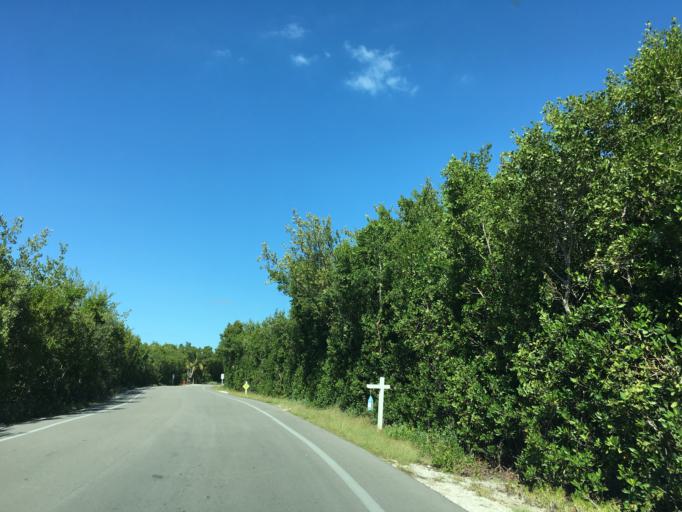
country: US
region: Florida
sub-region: Lee County
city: Pine Island Center
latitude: 26.5302
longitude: -82.1933
